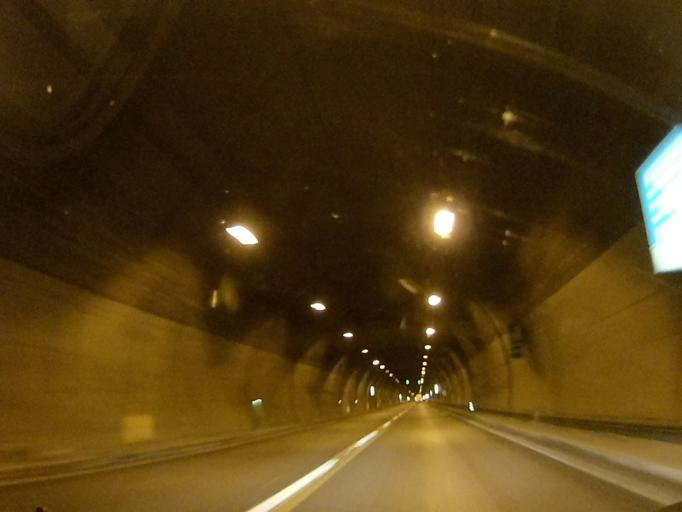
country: IT
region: Lombardy
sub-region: Provincia di Lecco
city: Dorio
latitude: 46.1093
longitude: 9.3332
